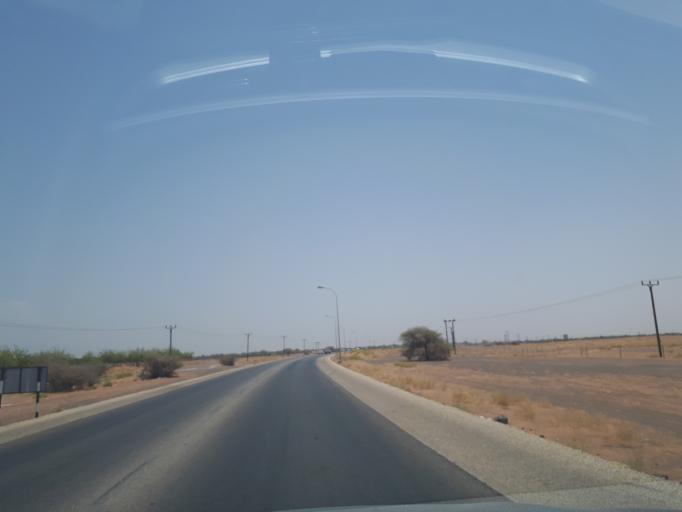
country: OM
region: Ash Sharqiyah
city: Badiyah
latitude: 22.4887
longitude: 58.7703
